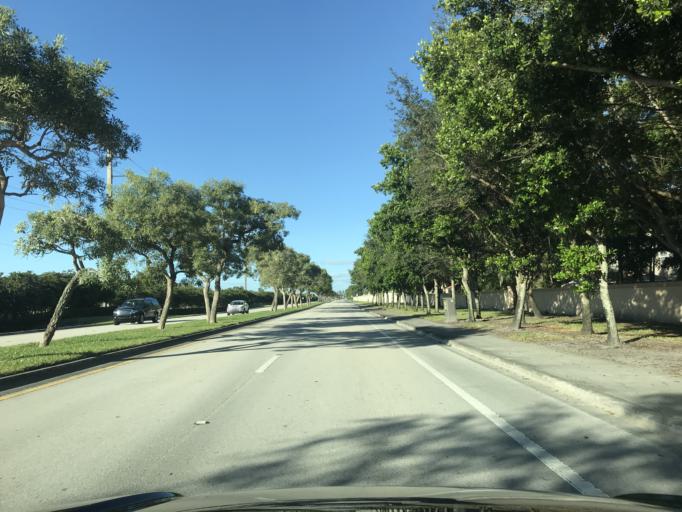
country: US
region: Florida
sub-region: Broward County
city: Pine Island Ridge
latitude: 26.1378
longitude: -80.2973
